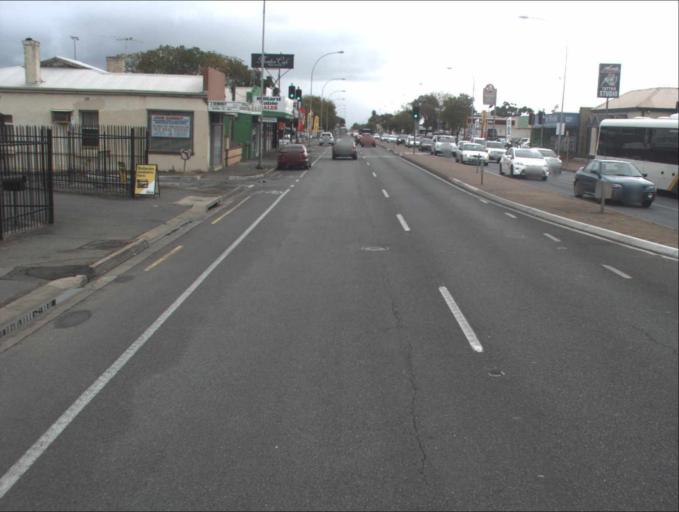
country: AU
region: South Australia
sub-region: Prospect
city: Prospect
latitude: -34.8877
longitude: 138.6030
